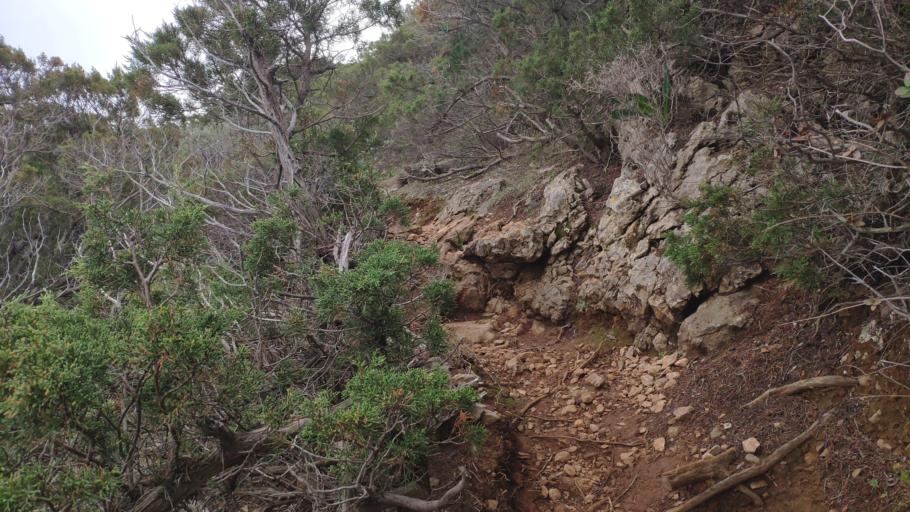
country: GR
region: Attica
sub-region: Nomarchia Anatolikis Attikis
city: Limin Mesoyaias
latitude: 37.9062
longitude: 24.0413
